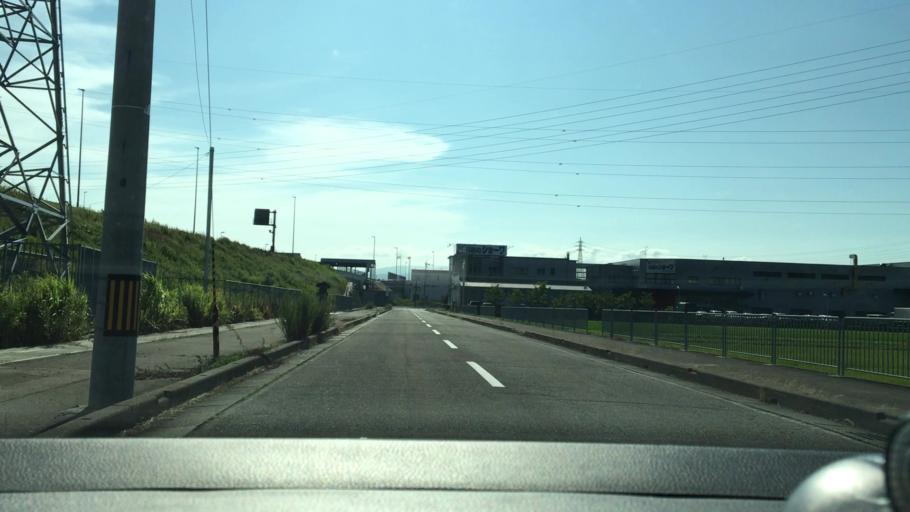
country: JP
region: Fukui
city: Fukui-shi
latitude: 36.0865
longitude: 136.2853
